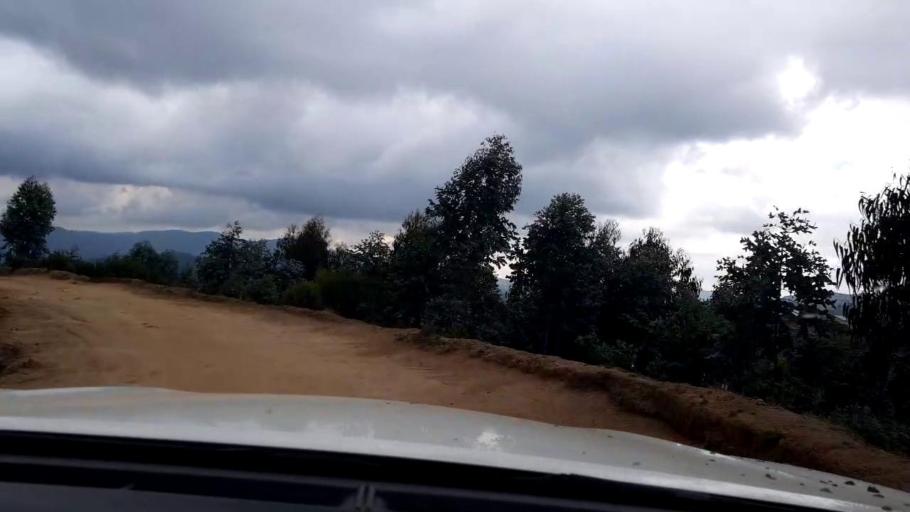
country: RW
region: Western Province
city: Kibuye
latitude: -1.8942
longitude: 29.5273
